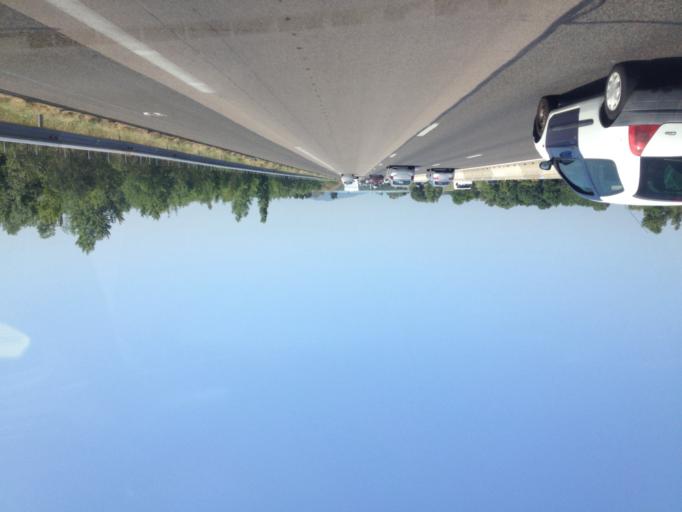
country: FR
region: Rhone-Alpes
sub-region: Departement de la Drome
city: Pierrelatte
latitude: 44.3787
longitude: 4.7323
